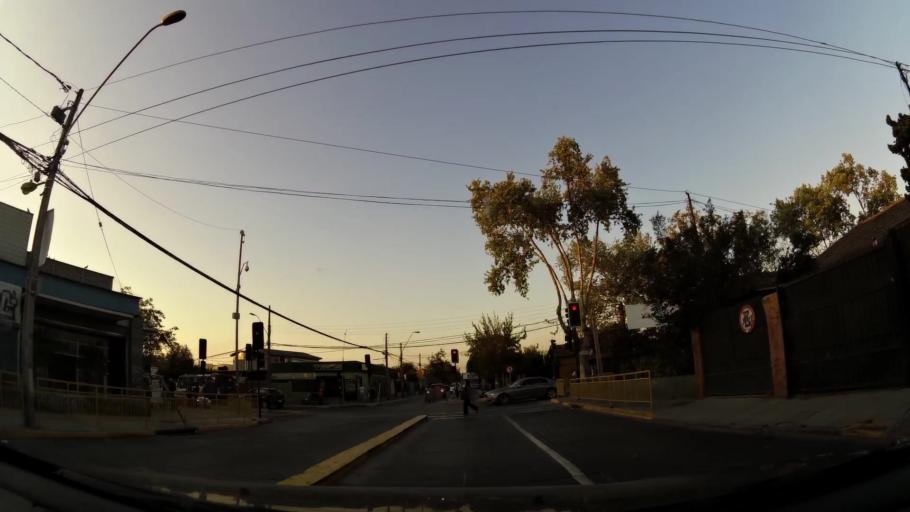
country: CL
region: Santiago Metropolitan
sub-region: Provincia de Santiago
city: La Pintana
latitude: -33.5466
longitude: -70.6667
